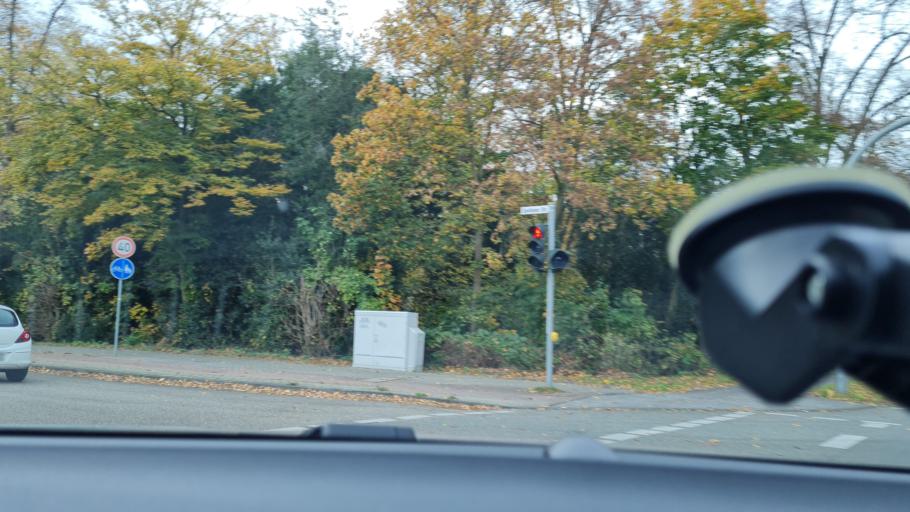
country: DE
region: North Rhine-Westphalia
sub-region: Regierungsbezirk Dusseldorf
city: Voerde
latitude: 51.6295
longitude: 6.6585
